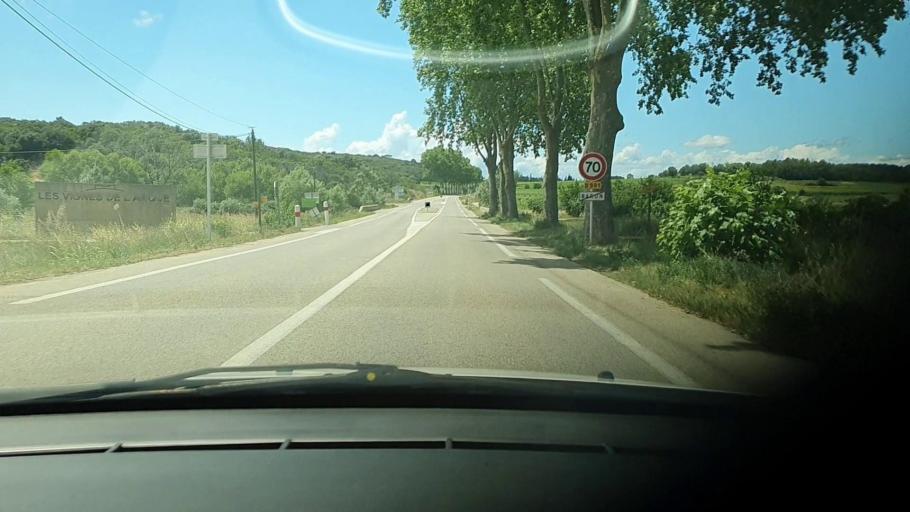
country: FR
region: Languedoc-Roussillon
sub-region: Departement du Gard
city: Saint-Chaptes
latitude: 44.0552
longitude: 4.2820
